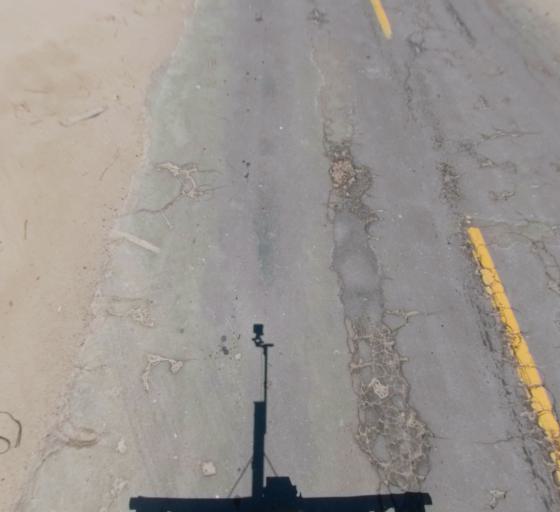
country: US
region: California
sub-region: Madera County
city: Parkwood
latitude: 36.8585
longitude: -120.1648
